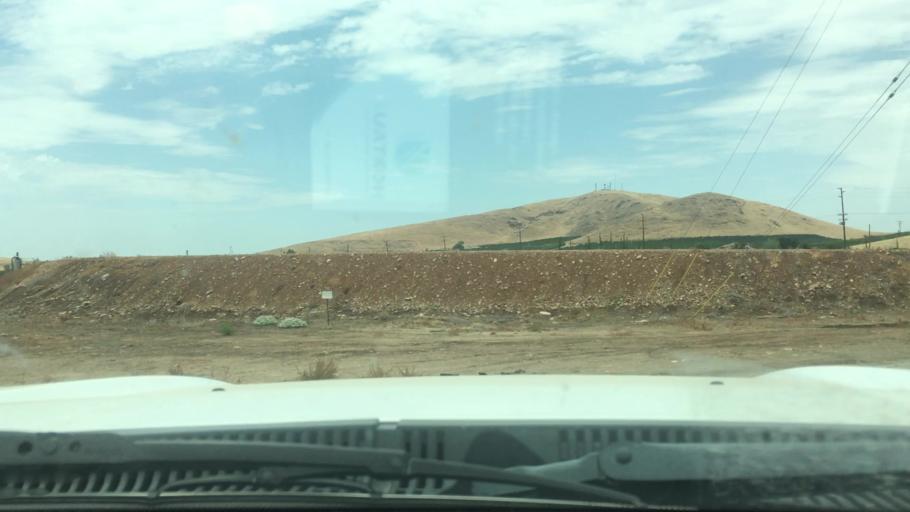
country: US
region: California
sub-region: Tulare County
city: Porterville
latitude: 36.0948
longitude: -119.0087
